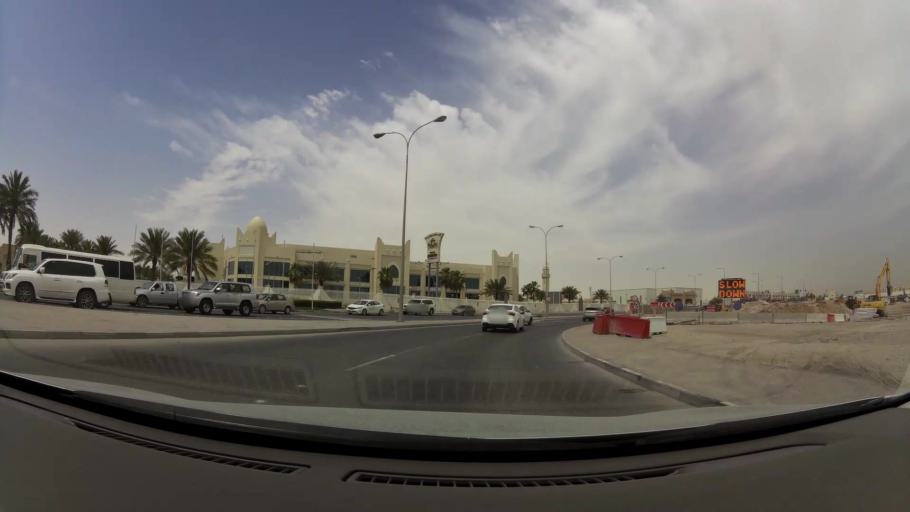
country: QA
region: Baladiyat ar Rayyan
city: Ar Rayyan
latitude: 25.2837
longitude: 51.4318
